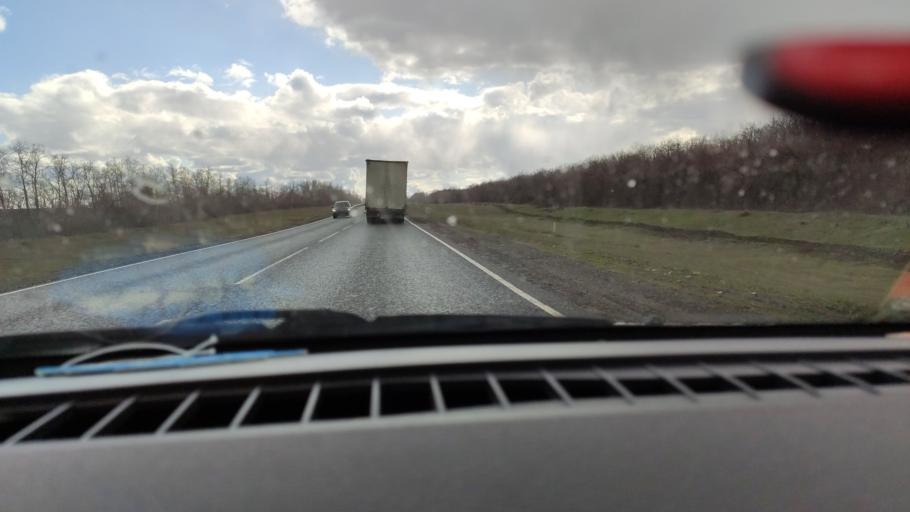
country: RU
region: Saratov
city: Balakovo
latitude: 52.1031
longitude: 47.7388
